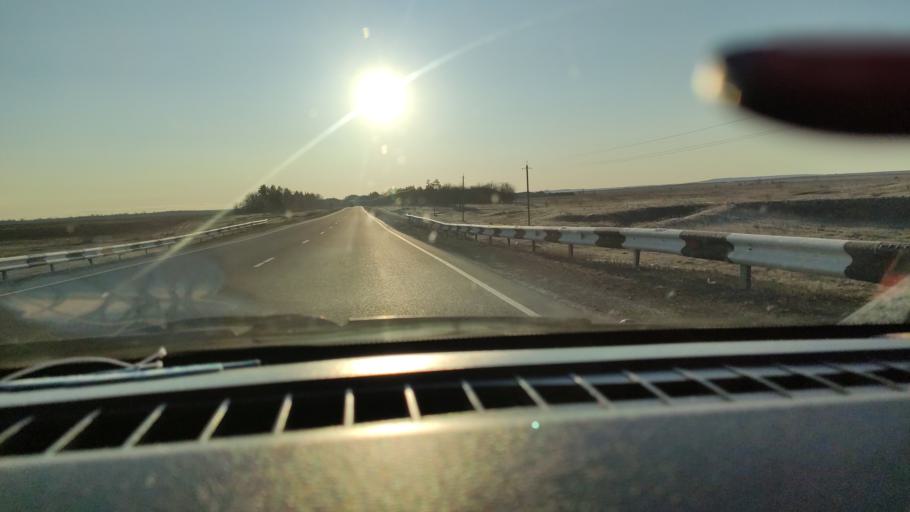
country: RU
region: Saratov
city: Sennoy
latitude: 52.1502
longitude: 46.9866
